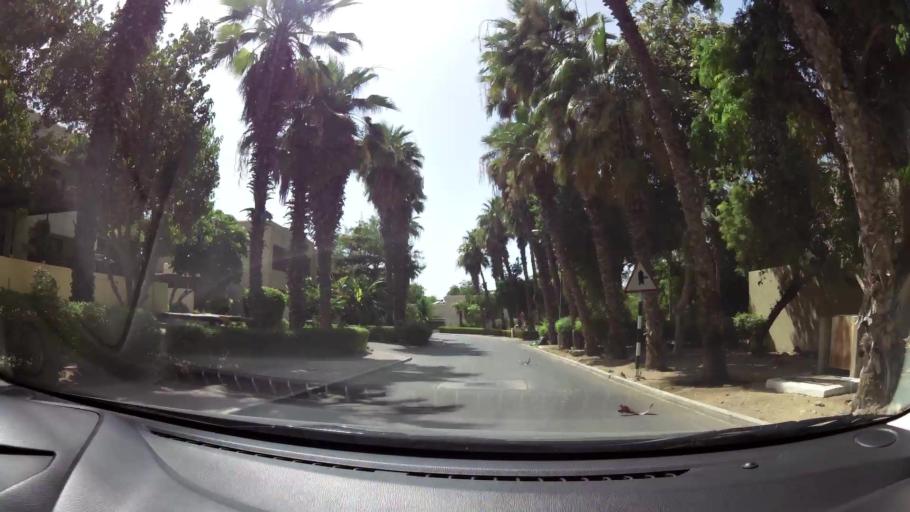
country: OM
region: Muhafazat Masqat
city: Muscat
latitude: 23.6319
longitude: 58.4944
